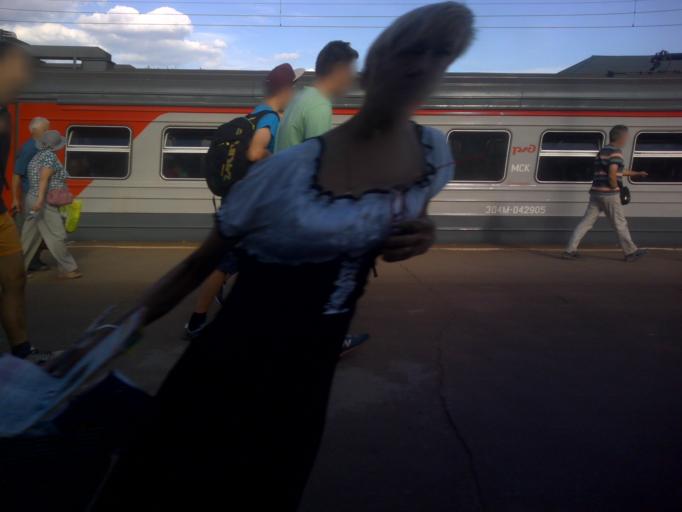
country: RU
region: Moscow
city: Nagornyy
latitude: 55.6553
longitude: 37.6225
